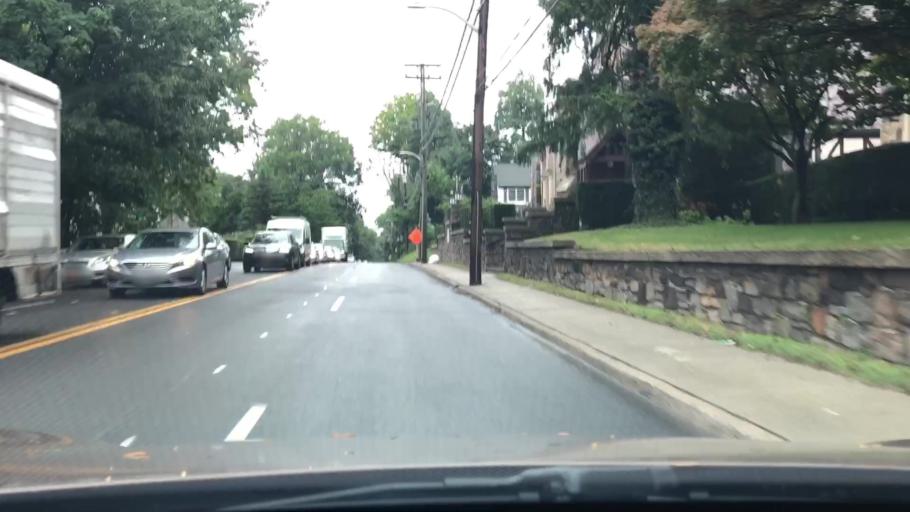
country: US
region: New York
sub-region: Westchester County
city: Greenville
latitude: 40.9814
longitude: -73.7998
